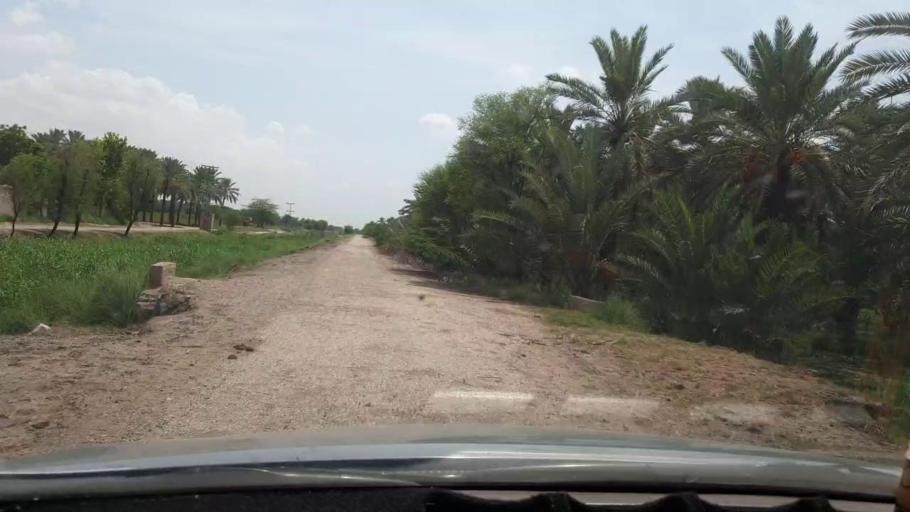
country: PK
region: Sindh
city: Khairpur
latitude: 27.4622
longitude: 68.7934
